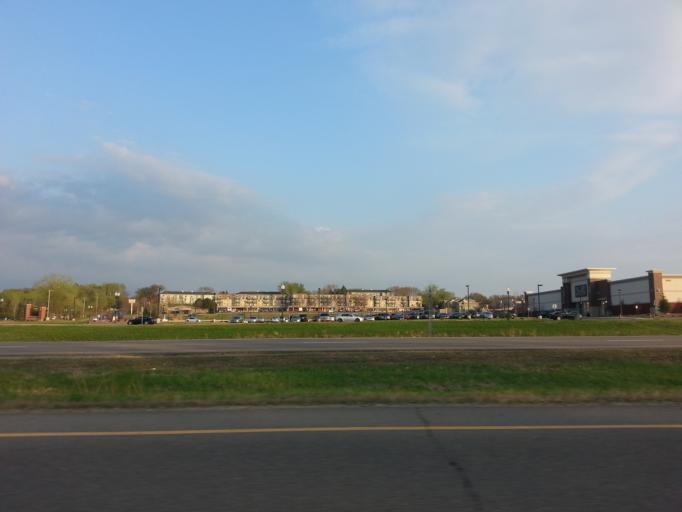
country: US
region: Minnesota
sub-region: Dakota County
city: Eagan
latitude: 44.8182
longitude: -93.2124
